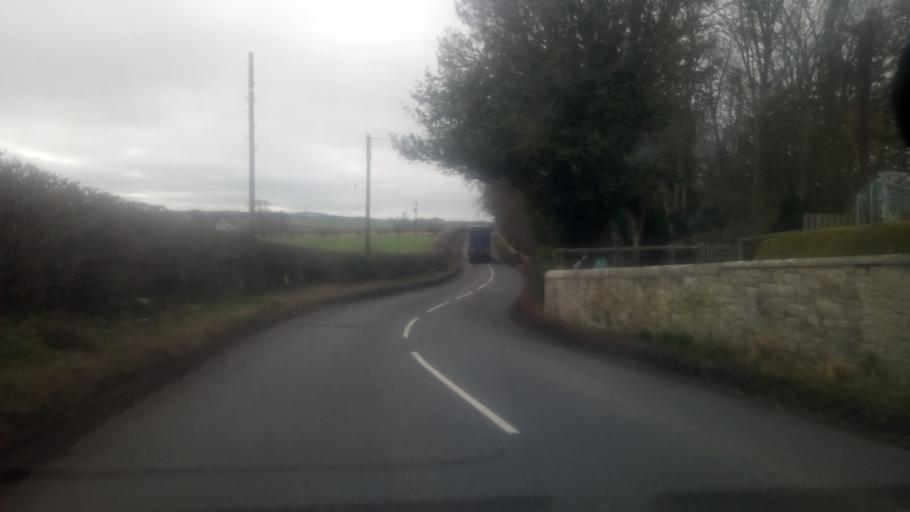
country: GB
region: Scotland
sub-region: The Scottish Borders
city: Kelso
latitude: 55.5934
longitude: -2.4638
